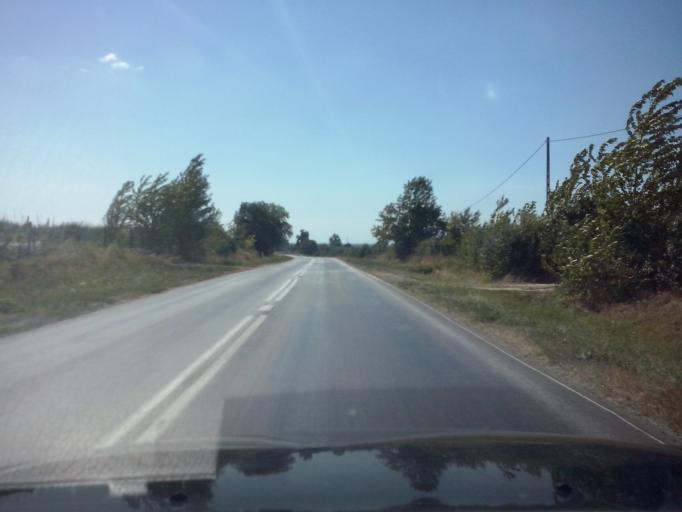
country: PL
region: Swietokrzyskie
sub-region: Powiat staszowski
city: Szydlow
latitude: 50.6099
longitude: 21.0090
